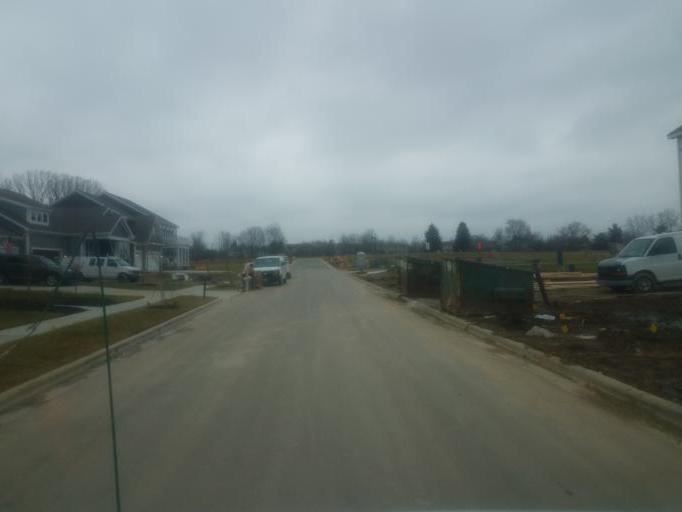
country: US
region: Ohio
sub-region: Franklin County
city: Westerville
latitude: 40.1313
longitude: -82.9634
